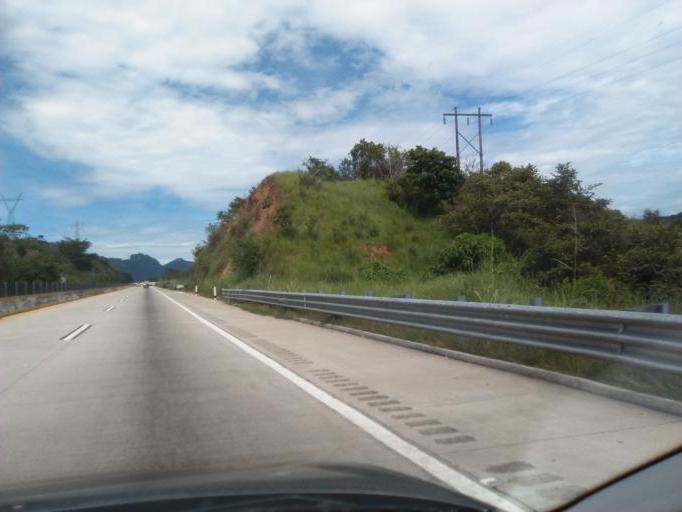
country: MX
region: Guerrero
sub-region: Chilpancingo de los Bravo
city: Julian Blanco (Dos Caminos)
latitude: 17.2293
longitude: -99.5251
